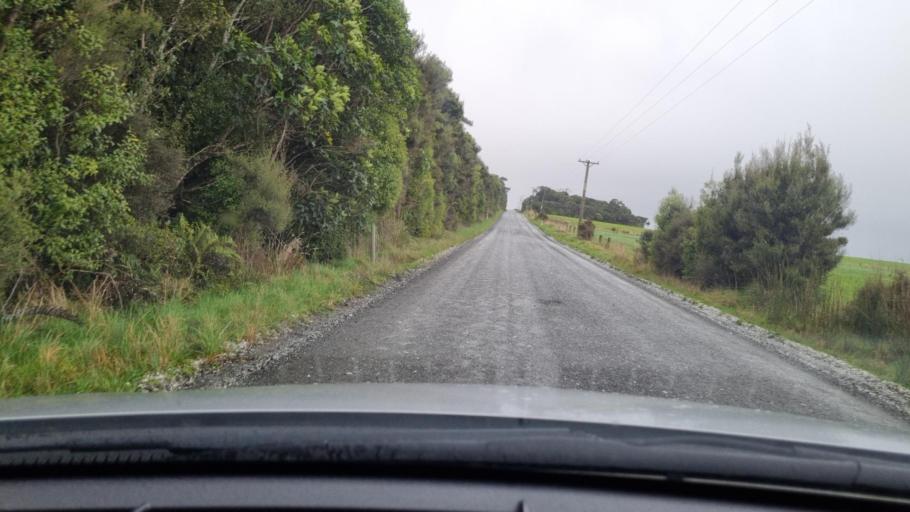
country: NZ
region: Southland
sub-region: Invercargill City
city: Bluff
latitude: -46.5309
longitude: 168.2680
